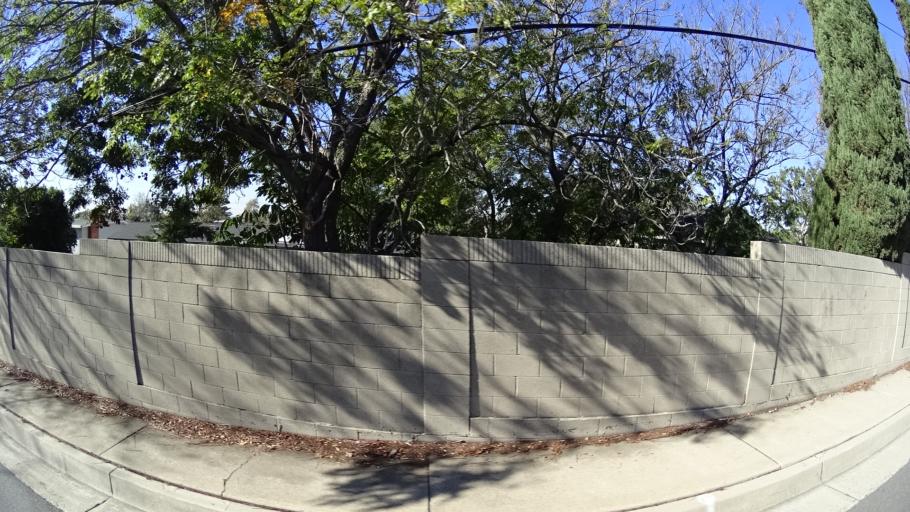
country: US
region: California
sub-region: Orange County
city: North Tustin
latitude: 33.7751
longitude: -117.8054
